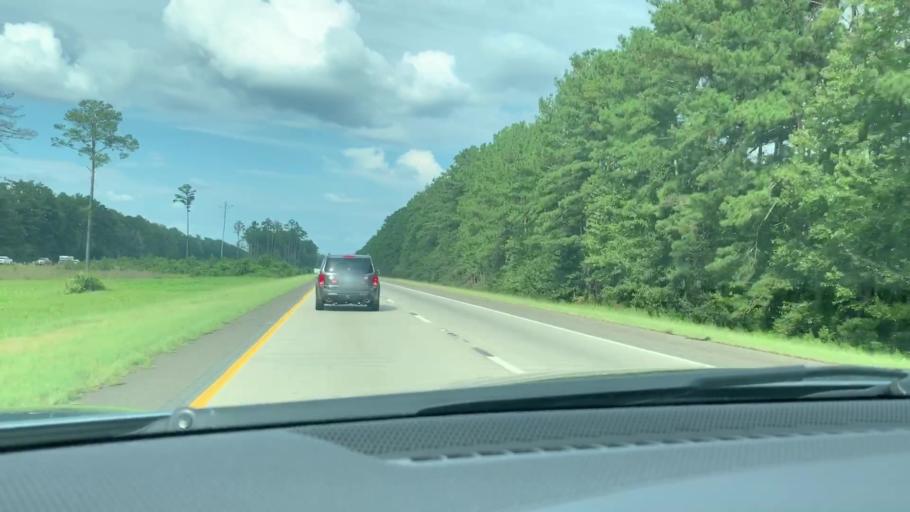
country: US
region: South Carolina
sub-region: Colleton County
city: Walterboro
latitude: 32.8528
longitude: -80.7329
